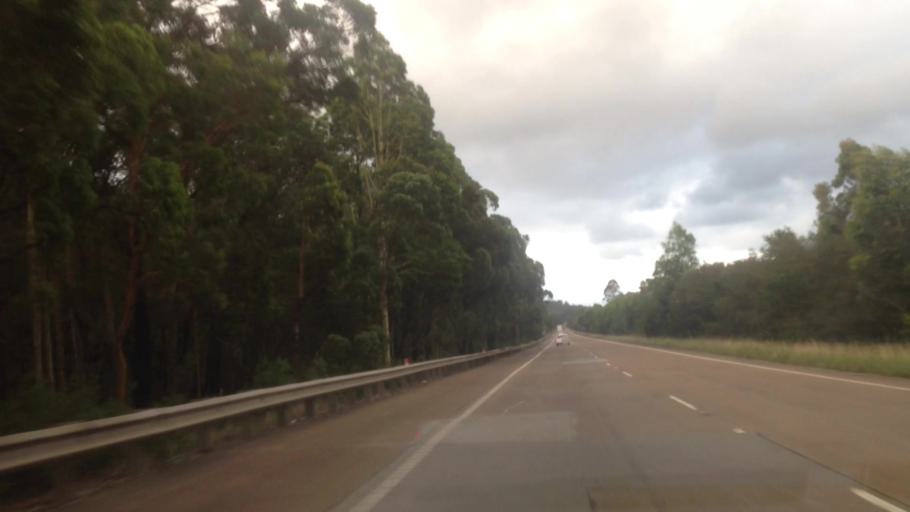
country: AU
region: New South Wales
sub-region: Wyong Shire
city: Charmhaven
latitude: -33.1689
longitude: 151.4673
